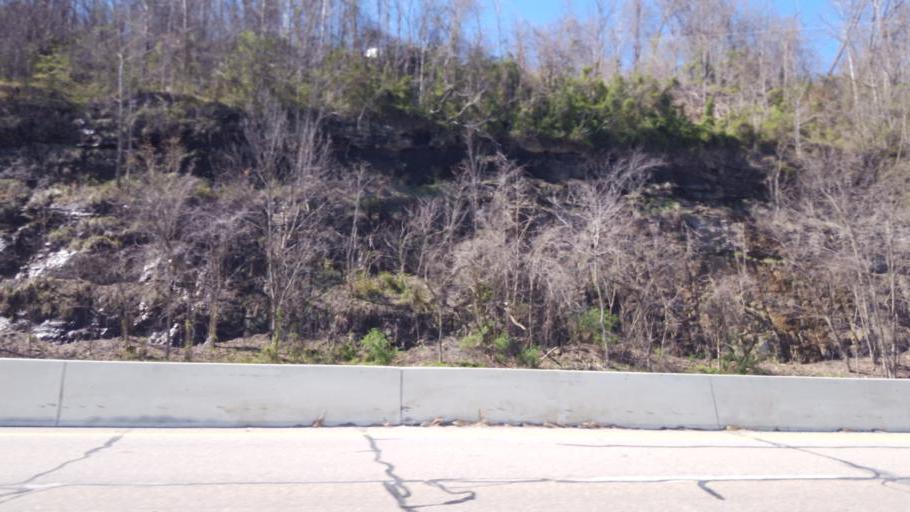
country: US
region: Ohio
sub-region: Jefferson County
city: Tiltonsville
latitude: 40.1774
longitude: -80.6969
